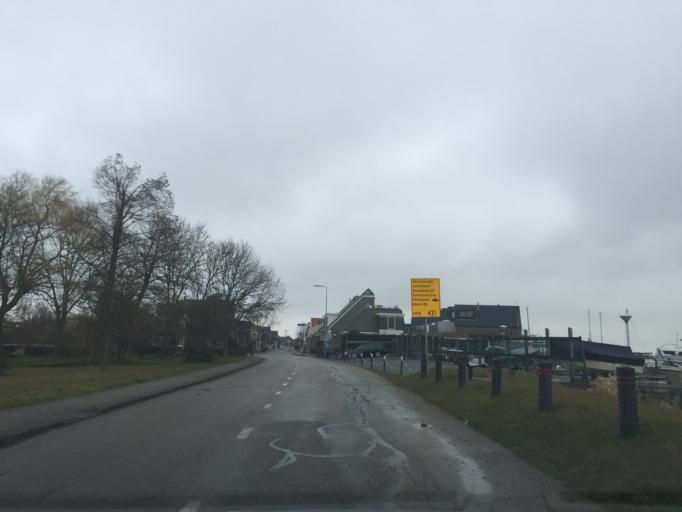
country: NL
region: South Holland
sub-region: Gemeente Kaag en Braassem
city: Oude Wetering
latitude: 52.2045
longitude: 4.6457
